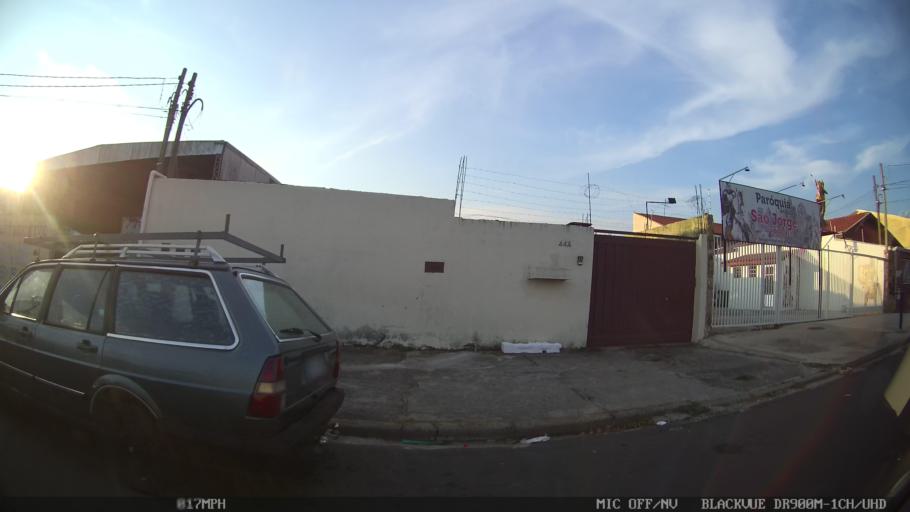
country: BR
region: Sao Paulo
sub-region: Campinas
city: Campinas
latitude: -22.9694
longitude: -47.1292
